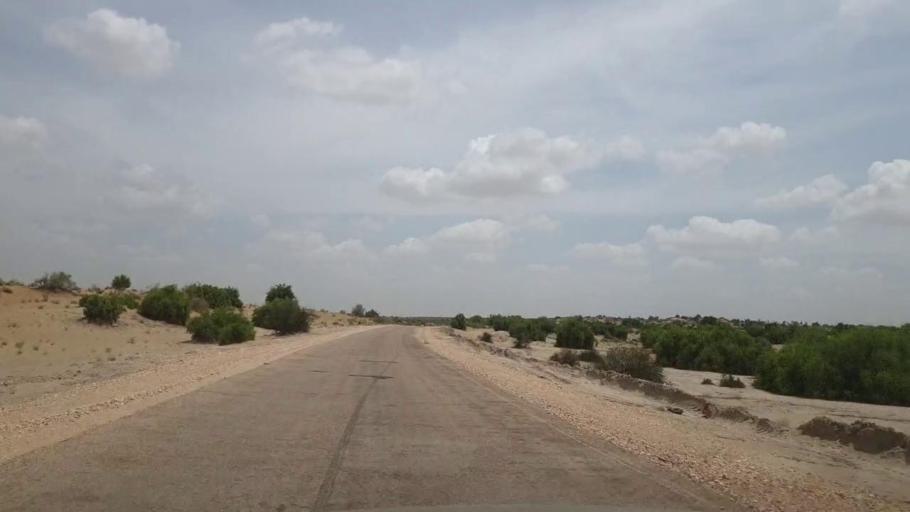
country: PK
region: Sindh
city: Kot Diji
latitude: 27.1870
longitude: 69.1704
